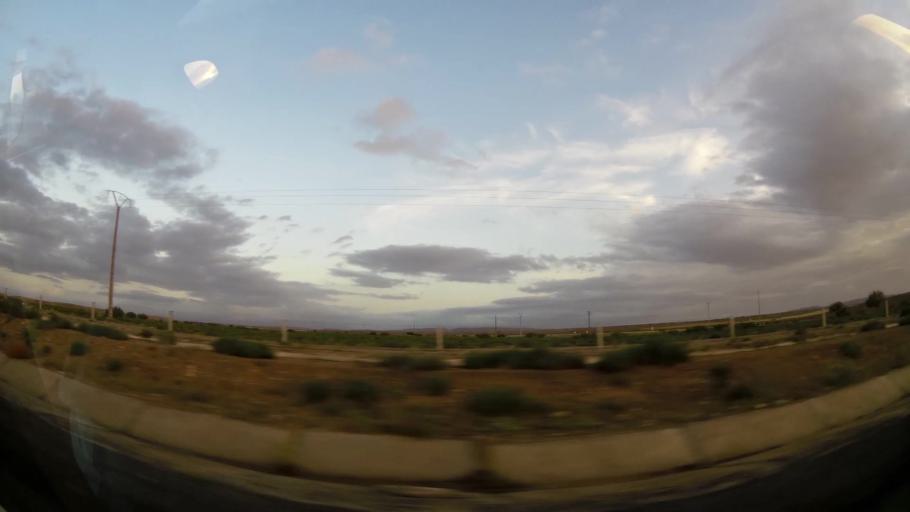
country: MA
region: Oriental
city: Taourirt
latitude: 34.5507
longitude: -2.8587
